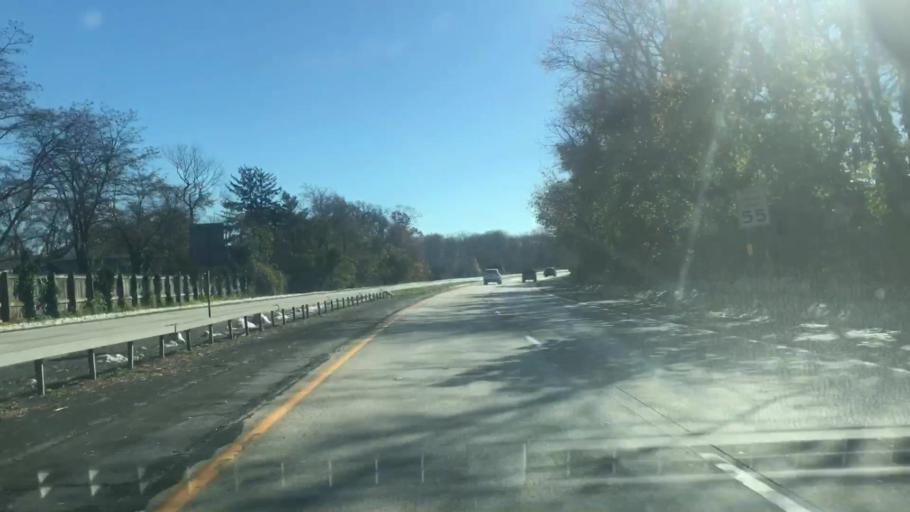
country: US
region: New York
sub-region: Suffolk County
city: North Babylon
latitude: 40.7252
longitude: -73.3167
